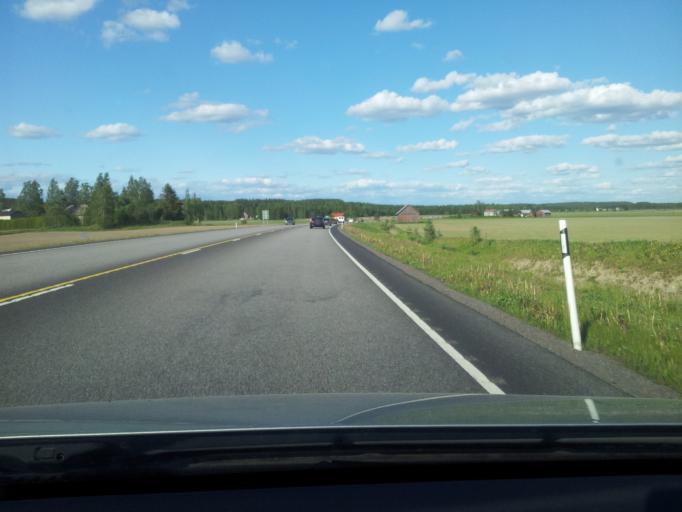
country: FI
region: Kymenlaakso
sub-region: Kouvola
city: Elimaeki
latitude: 60.7069
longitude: 26.3202
